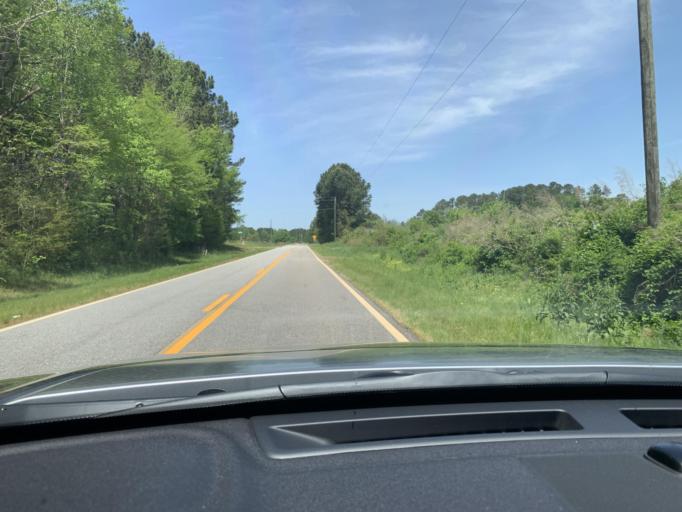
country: US
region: Georgia
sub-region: Oconee County
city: Bogart
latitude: 33.8678
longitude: -83.5686
